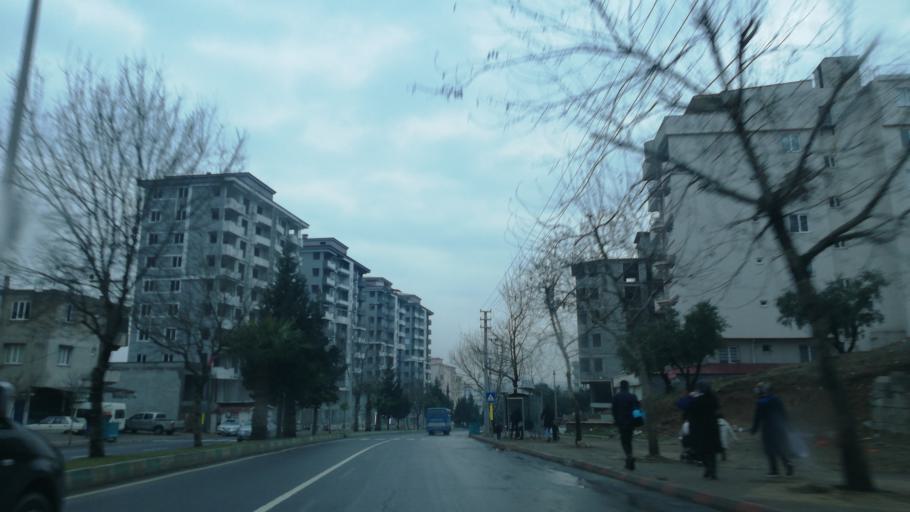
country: TR
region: Kahramanmaras
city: Kahramanmaras
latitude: 37.5819
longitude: 36.9699
